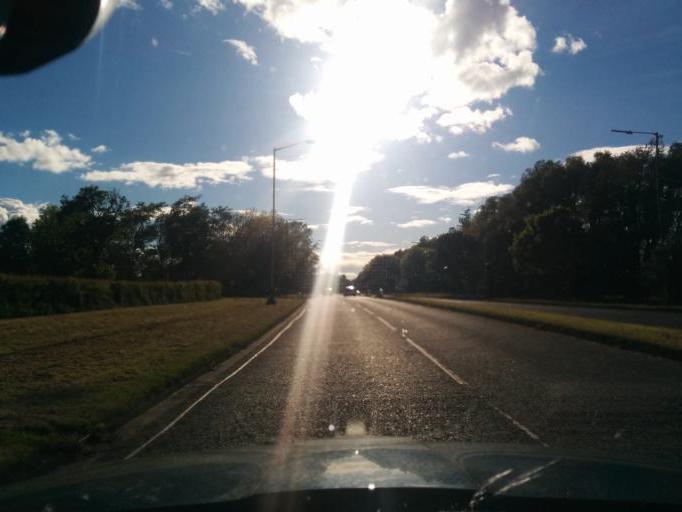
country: GB
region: England
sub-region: Northumberland
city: Cramlington
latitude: 55.0875
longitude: -1.6029
